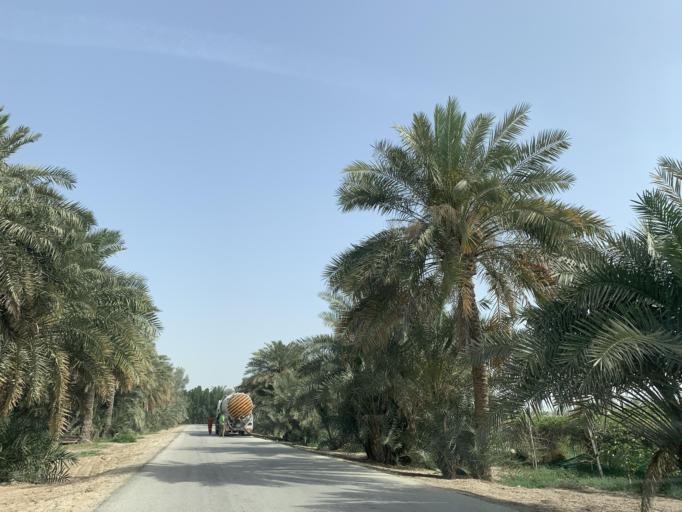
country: BH
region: Northern
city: Madinat `Isa
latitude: 26.1661
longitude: 50.5335
